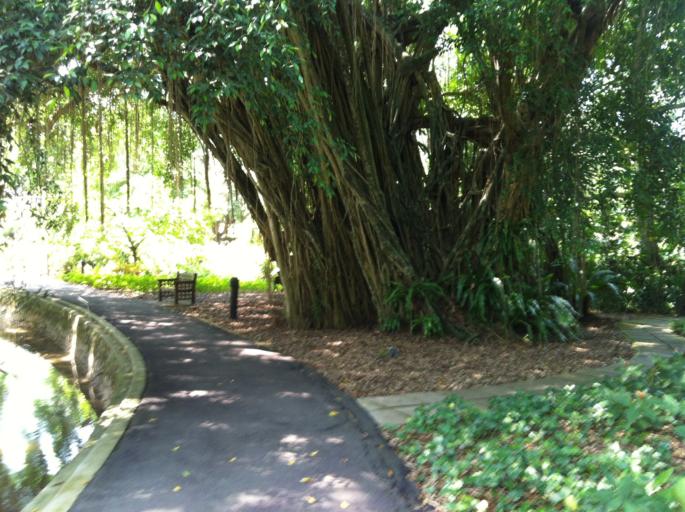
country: SG
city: Singapore
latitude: 1.3070
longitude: 103.8161
